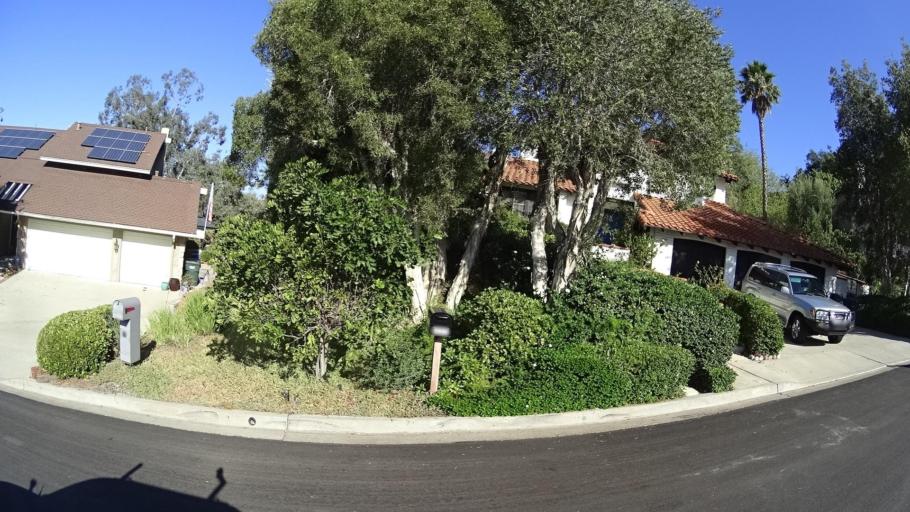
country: US
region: California
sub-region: San Diego County
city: Casa de Oro-Mount Helix
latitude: 32.7647
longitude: -116.9904
